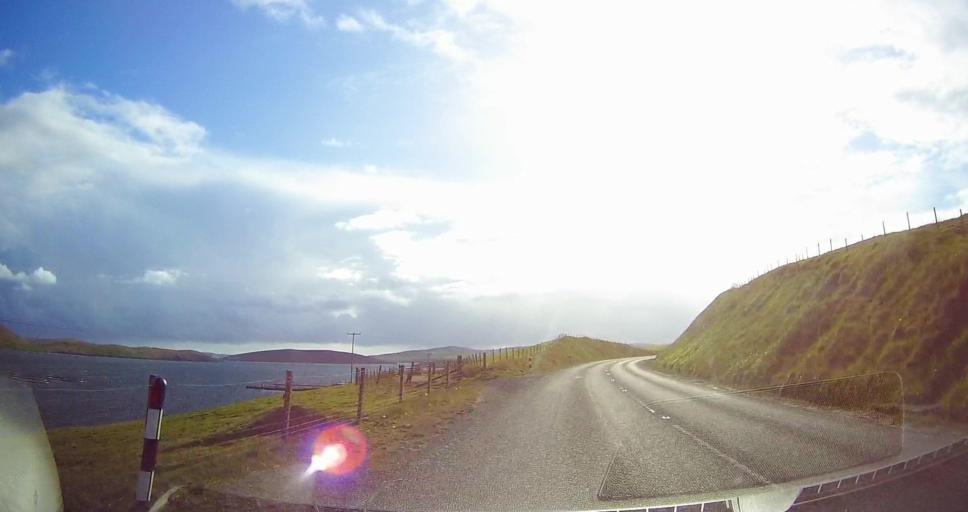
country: GB
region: Scotland
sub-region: Shetland Islands
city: Lerwick
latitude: 60.3705
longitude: -1.3073
